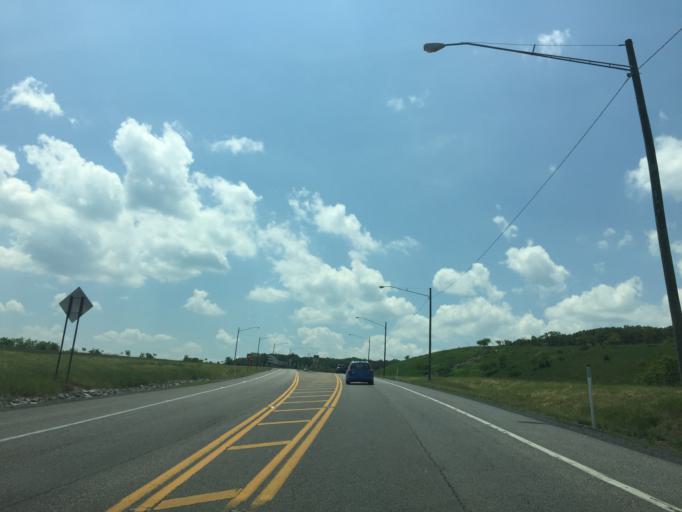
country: US
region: Virginia
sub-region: Shenandoah County
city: Woodstock
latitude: 39.0739
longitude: -78.6277
